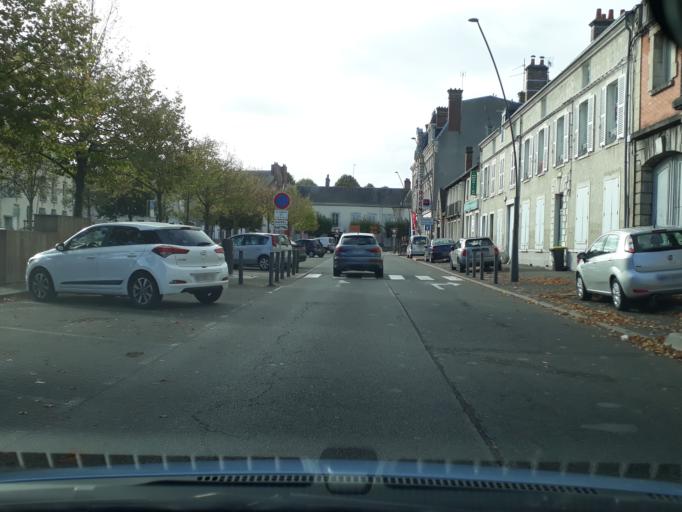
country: FR
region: Centre
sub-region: Departement du Loiret
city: Pithiviers
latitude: 48.1732
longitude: 2.2532
